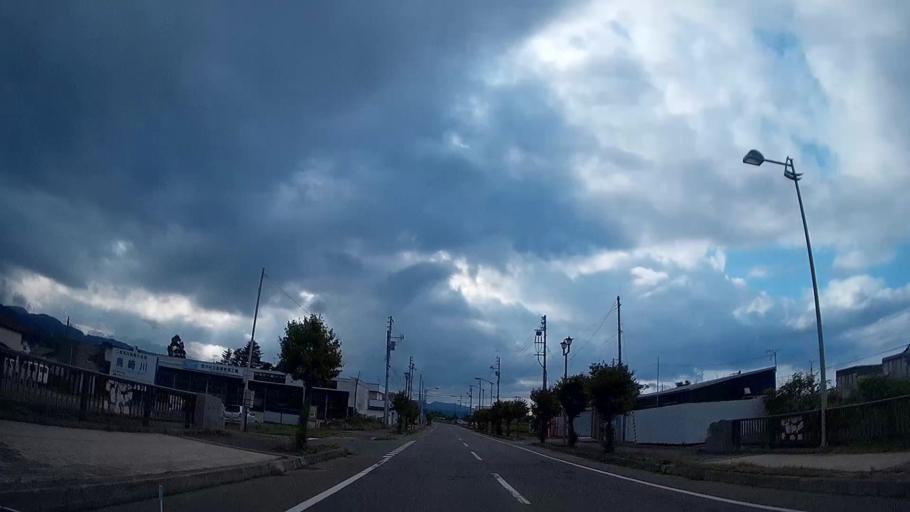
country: JP
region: Hokkaido
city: Nanae
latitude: 42.1095
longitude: 140.5682
